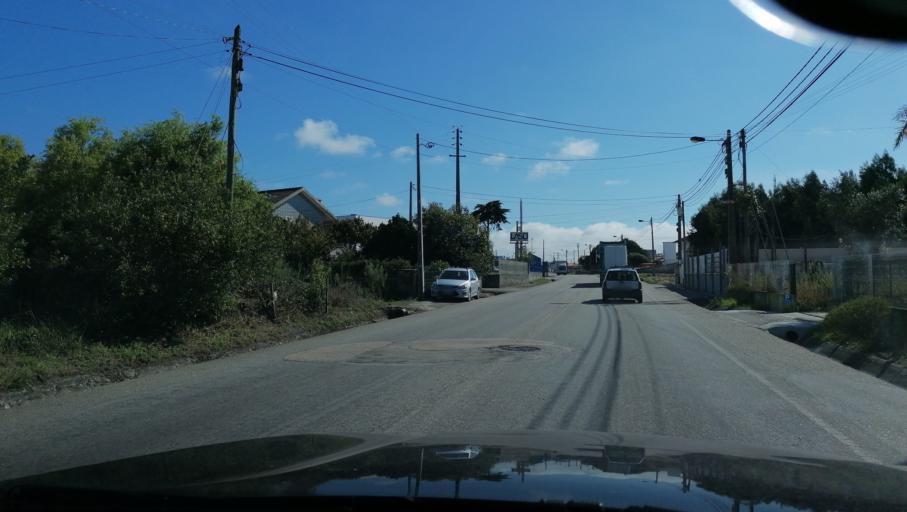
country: PT
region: Aveiro
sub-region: Aveiro
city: Aveiro
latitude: 40.6723
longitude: -8.6047
